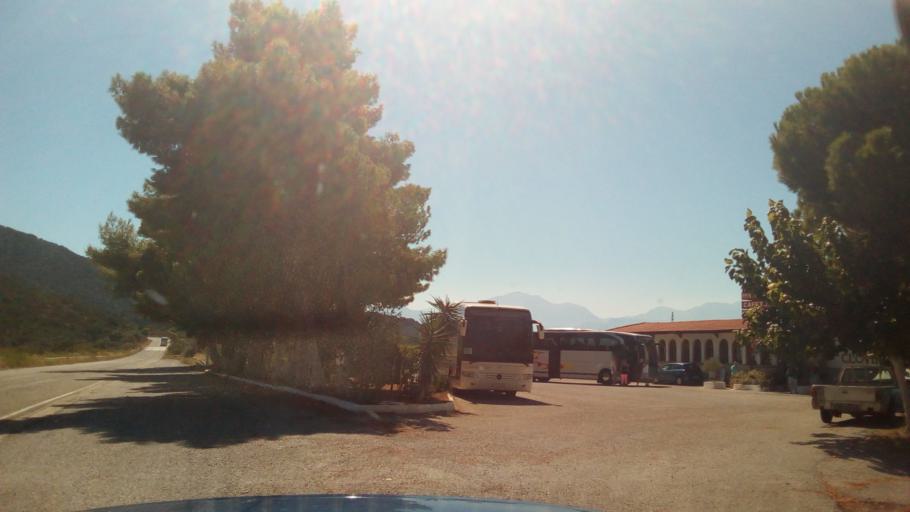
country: GR
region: West Greece
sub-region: Nomos Achaias
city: Aigio
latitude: 38.3559
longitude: 22.1398
